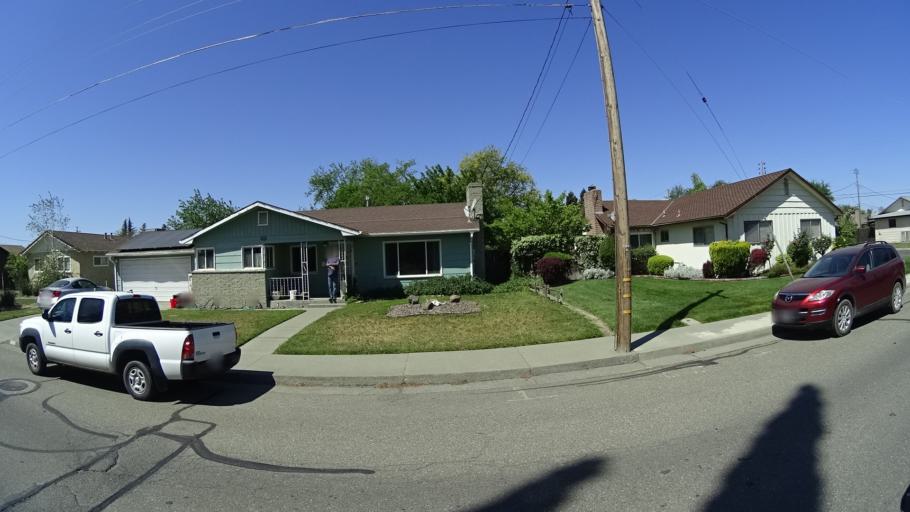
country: US
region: California
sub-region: Glenn County
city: Orland
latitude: 39.7527
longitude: -122.1994
